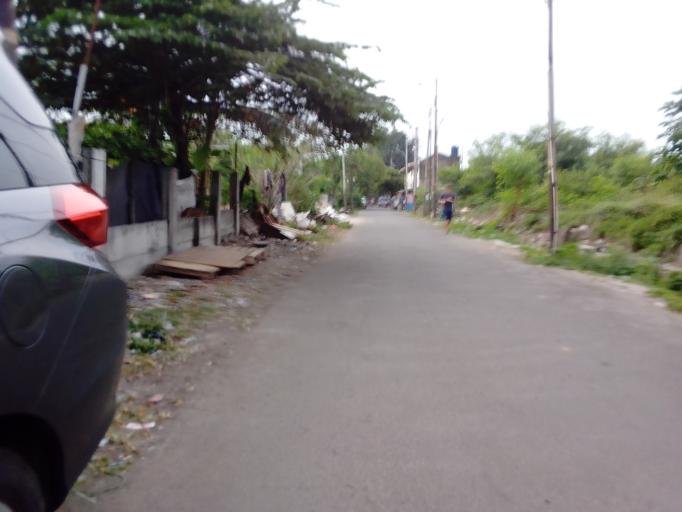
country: ID
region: Jakarta Raya
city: Jakarta
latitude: -6.1644
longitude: 106.8029
